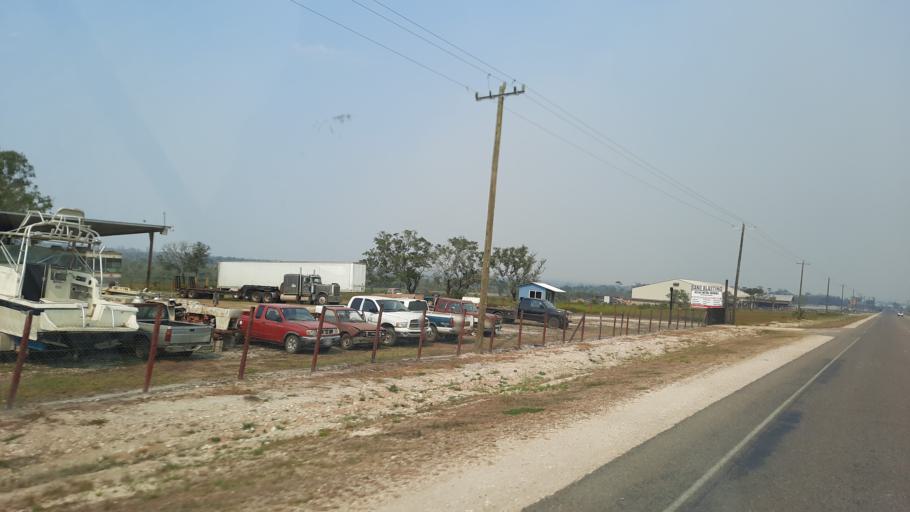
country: BZ
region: Cayo
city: Valley of Peace
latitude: 17.2440
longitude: -88.9541
